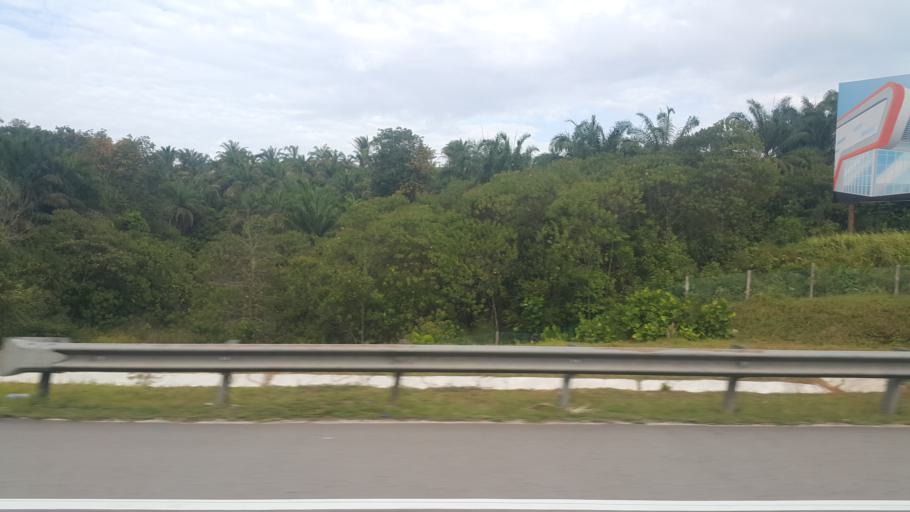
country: MY
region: Johor
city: Pekan Nenas
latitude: 1.4244
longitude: 103.6019
